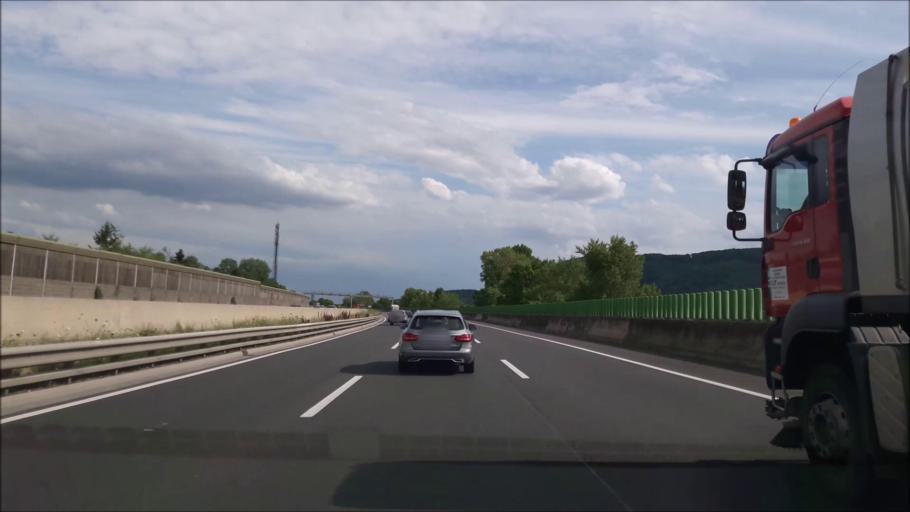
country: AT
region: Lower Austria
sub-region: Politischer Bezirk Korneuburg
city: Langenzersdorf
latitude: 48.3049
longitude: 16.3456
